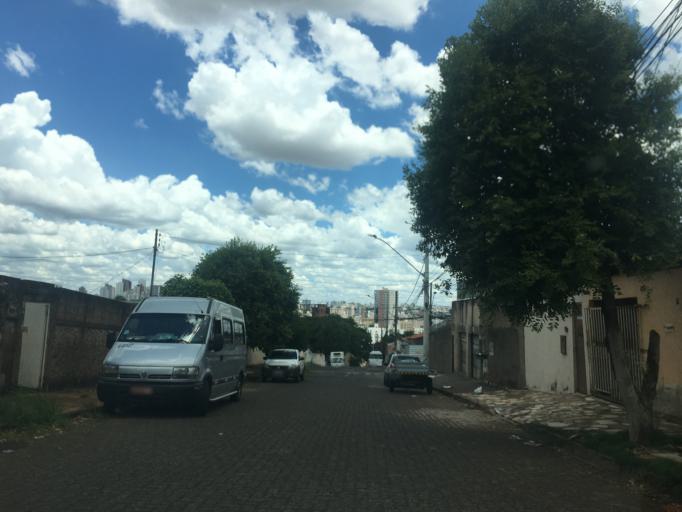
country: BR
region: Minas Gerais
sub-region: Uberlandia
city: Uberlandia
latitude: -18.9317
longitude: -48.3011
